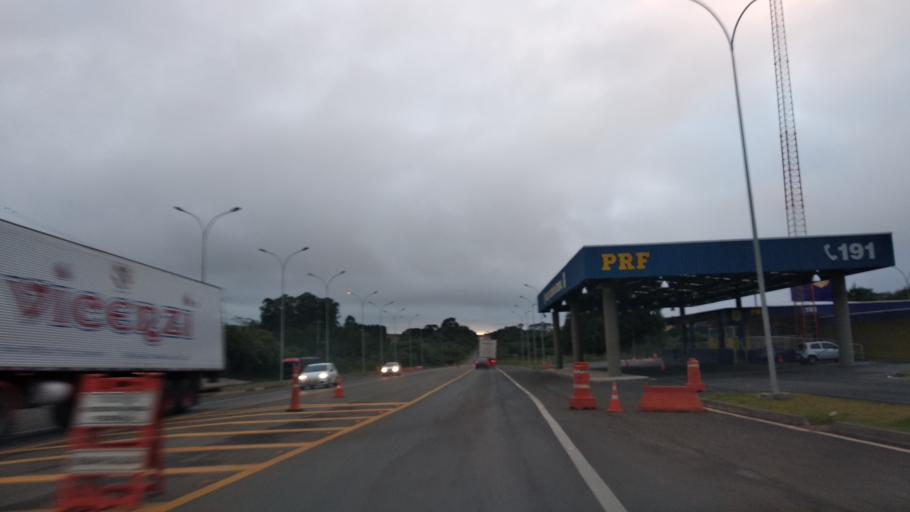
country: BR
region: Santa Catarina
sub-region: Campos Novos
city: Campos Novos
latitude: -27.3874
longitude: -51.1144
